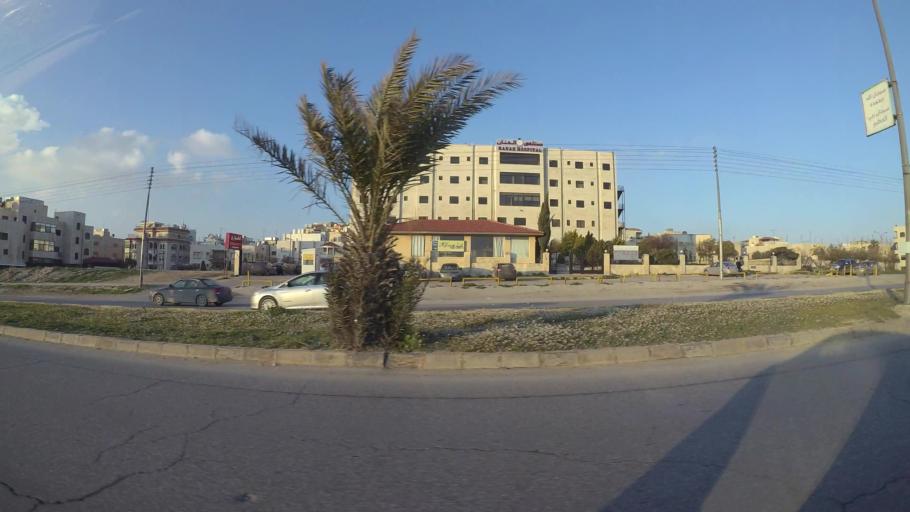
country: JO
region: Amman
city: Al Quwaysimah
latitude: 31.9086
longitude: 35.9287
